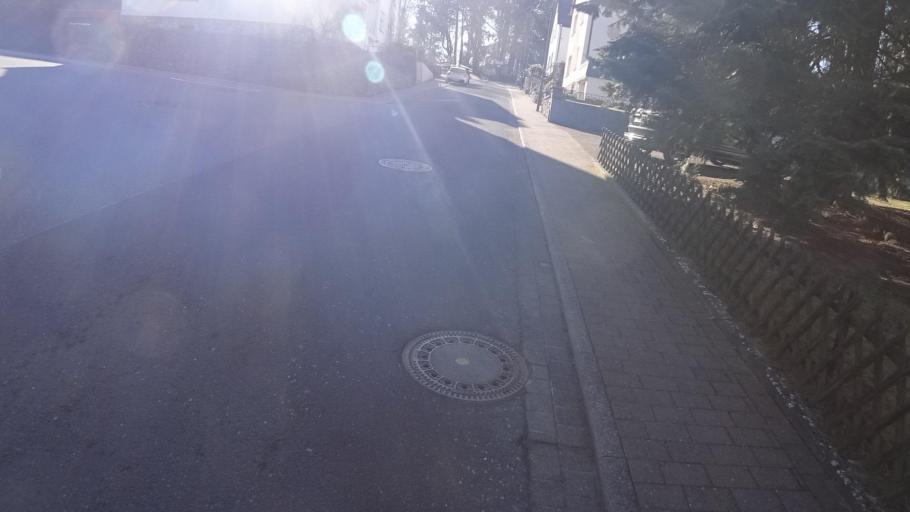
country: DE
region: Rheinland-Pfalz
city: Simmern
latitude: 49.9794
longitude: 7.5257
